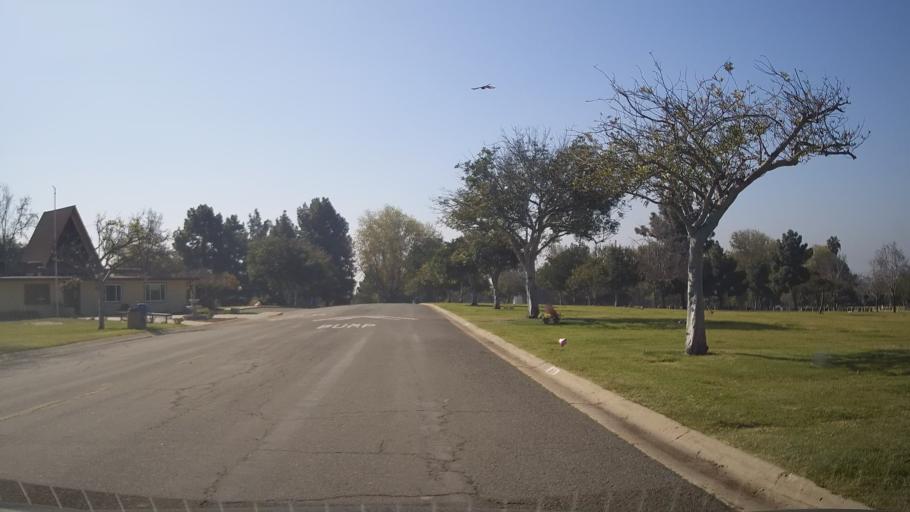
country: US
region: California
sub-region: San Diego County
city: National City
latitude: 32.7101
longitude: -117.1126
